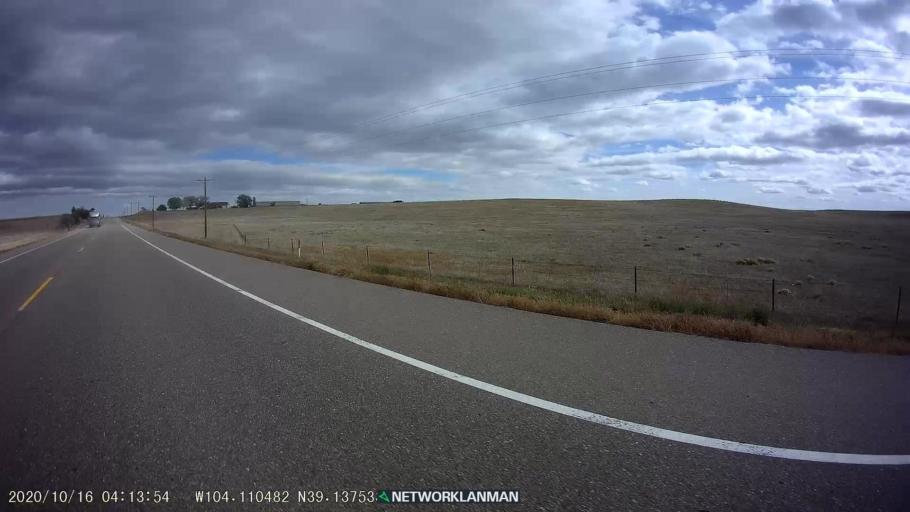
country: US
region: Colorado
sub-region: El Paso County
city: Ellicott
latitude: 39.1374
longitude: -104.1102
